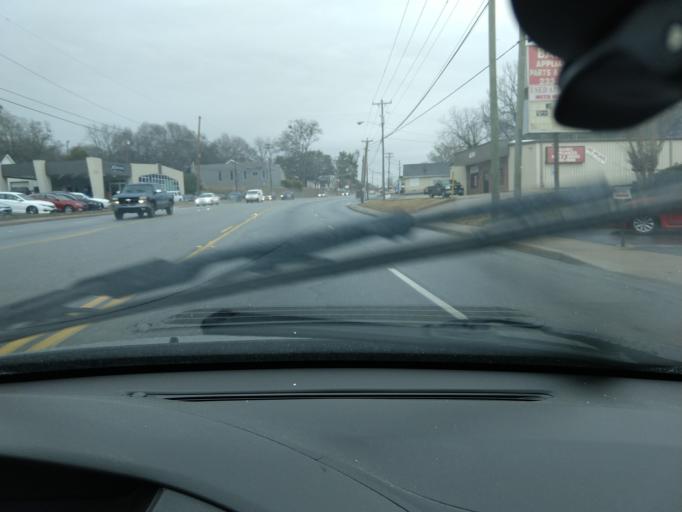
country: US
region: South Carolina
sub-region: Greenville County
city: Greenville
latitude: 34.8503
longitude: -82.3756
